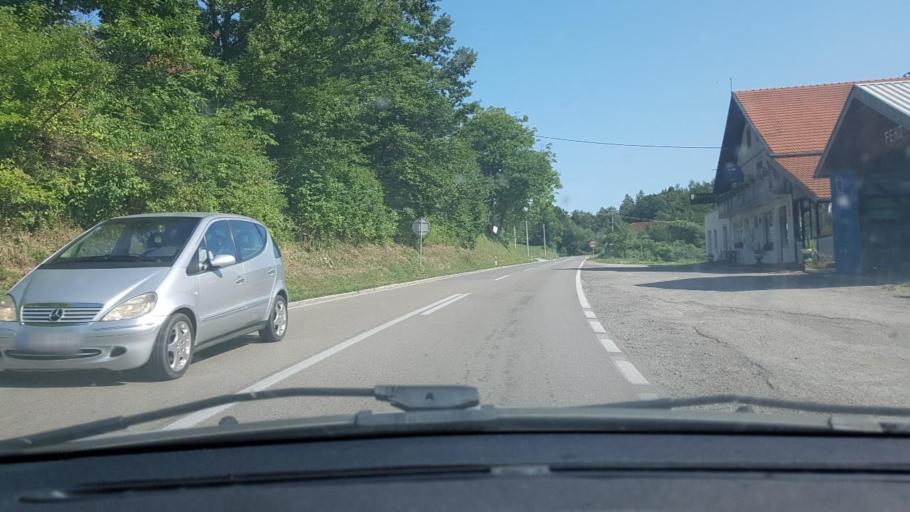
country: BA
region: Federation of Bosnia and Herzegovina
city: Skokovi
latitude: 45.0175
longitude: 15.9035
